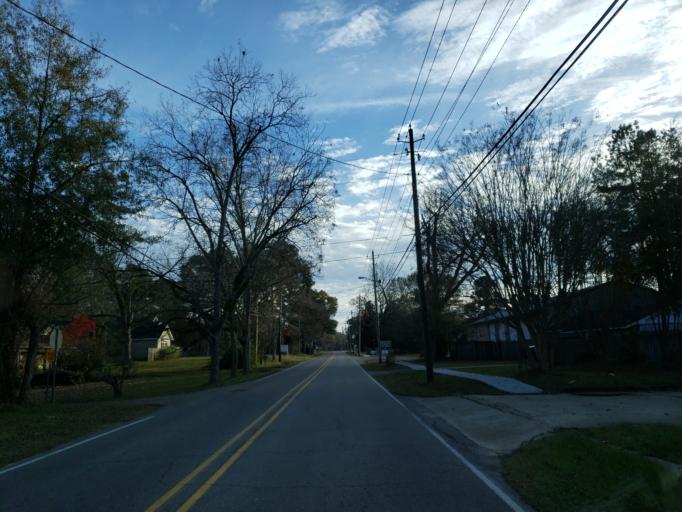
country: US
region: Mississippi
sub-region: Lamar County
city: Purvis
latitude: 31.1522
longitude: -89.4117
